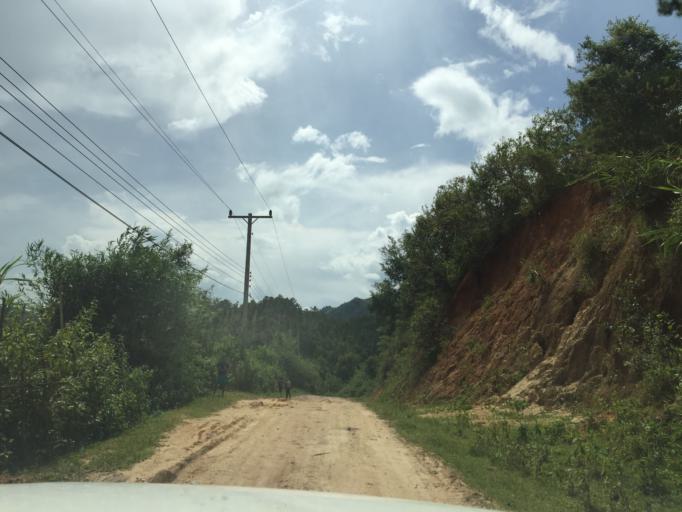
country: LA
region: Xiangkhoang
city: Muang Phonsavan
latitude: 19.3408
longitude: 103.5388
